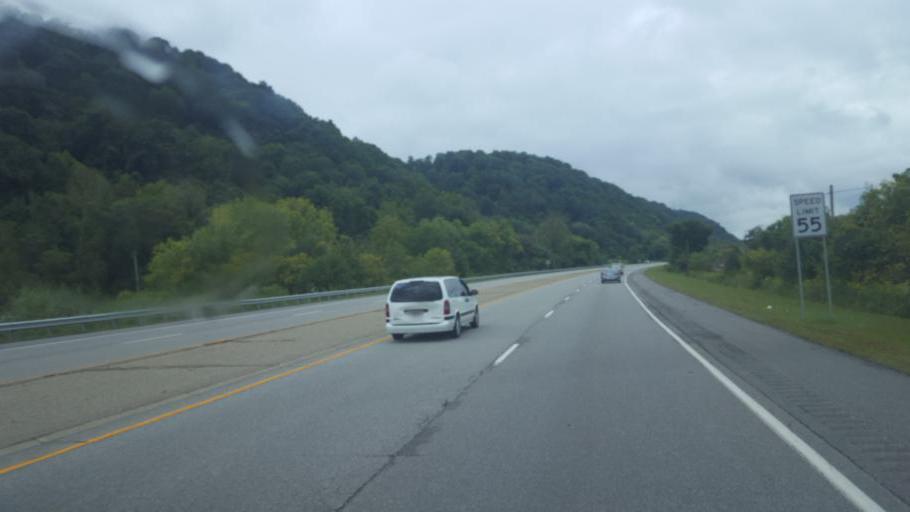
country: US
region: Kentucky
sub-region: Greenup County
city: South Shore
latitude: 38.7204
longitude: -82.9693
